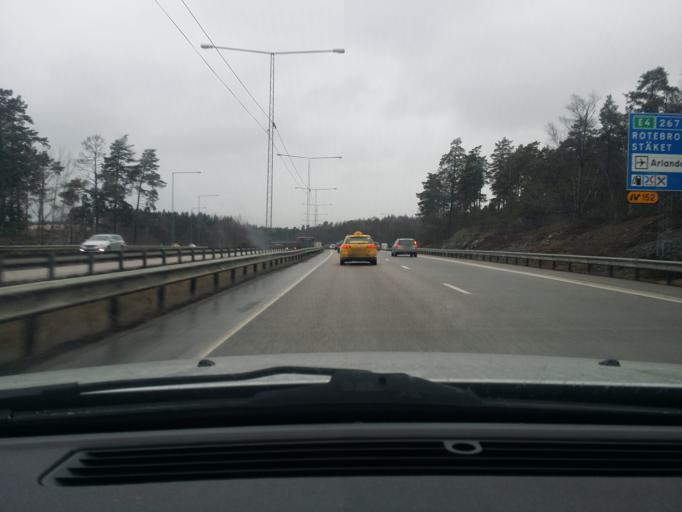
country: SE
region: Stockholm
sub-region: Jarfalla Kommun
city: Jakobsberg
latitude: 59.4684
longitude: 17.8172
